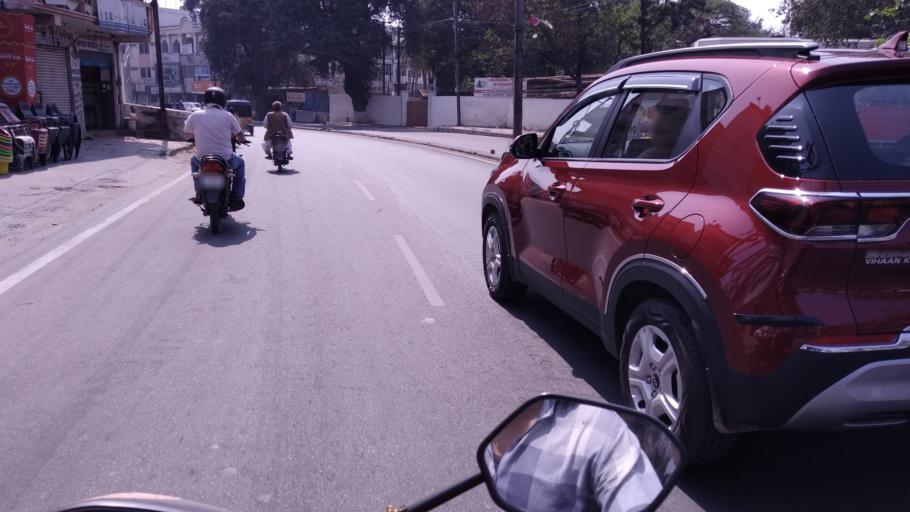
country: IN
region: Telangana
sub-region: Rangareddi
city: Quthbullapur
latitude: 17.4601
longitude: 78.4759
